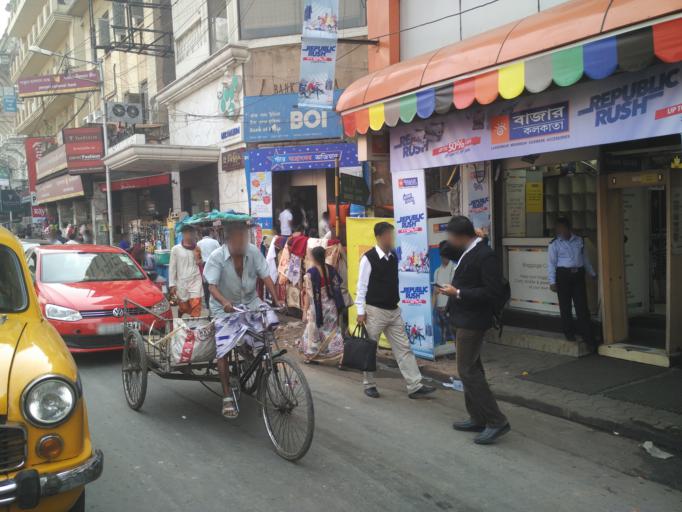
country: IN
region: West Bengal
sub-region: Kolkata
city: Bara Bazar
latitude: 22.5593
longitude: 88.3529
